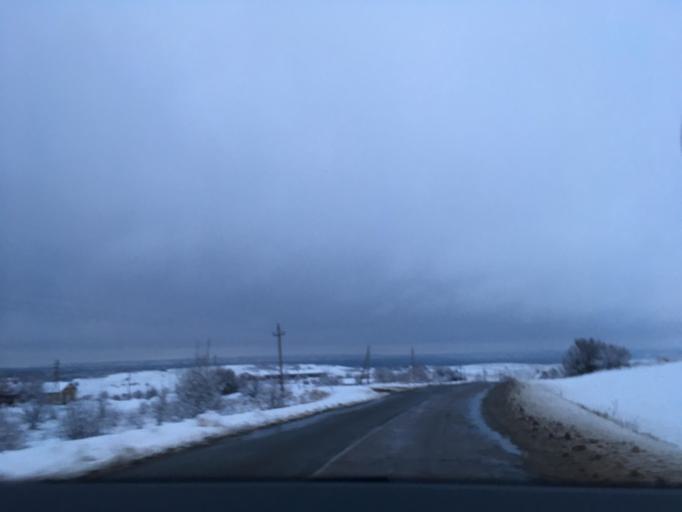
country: RU
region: Voronezj
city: Verkhniy Mamon
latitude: 50.0729
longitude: 40.2920
